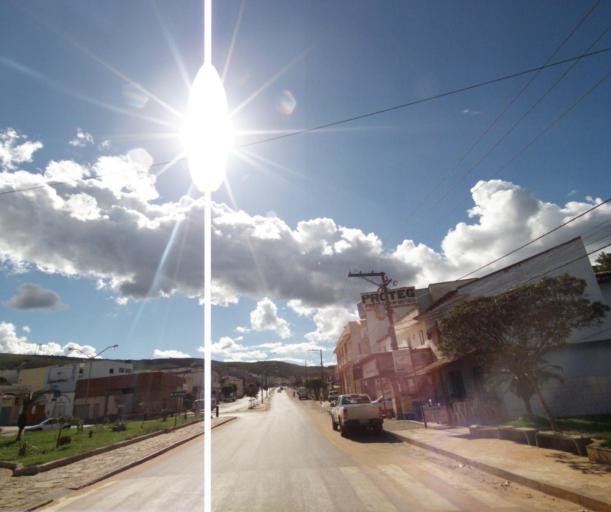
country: BR
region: Bahia
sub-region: Caetite
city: Caetite
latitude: -14.0648
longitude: -42.4900
